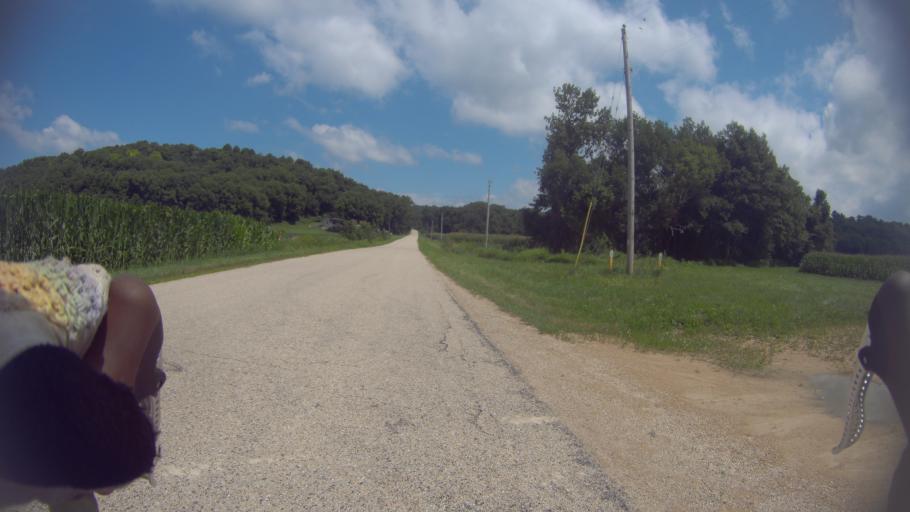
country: US
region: Wisconsin
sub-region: Dane County
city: Cross Plains
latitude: 43.2213
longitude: -89.6206
